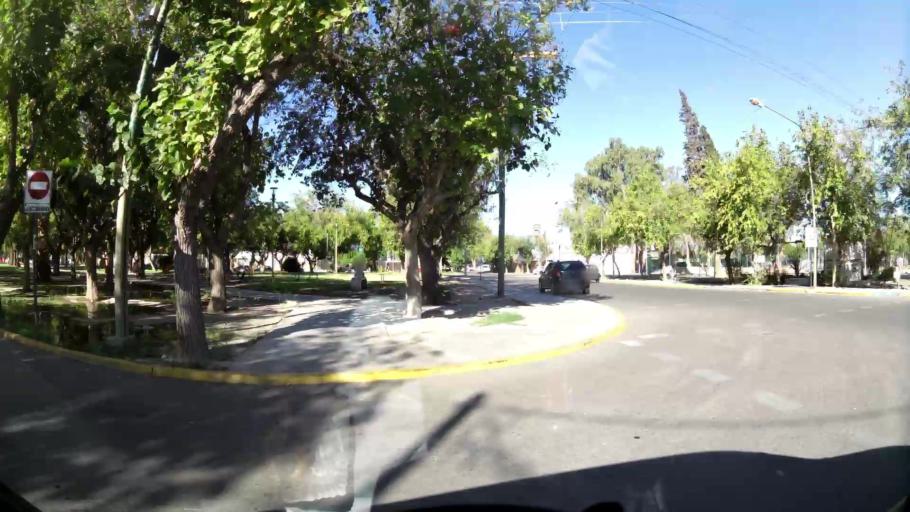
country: AR
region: San Juan
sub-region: Departamento de Santa Lucia
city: Santa Lucia
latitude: -31.5369
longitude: -68.5098
